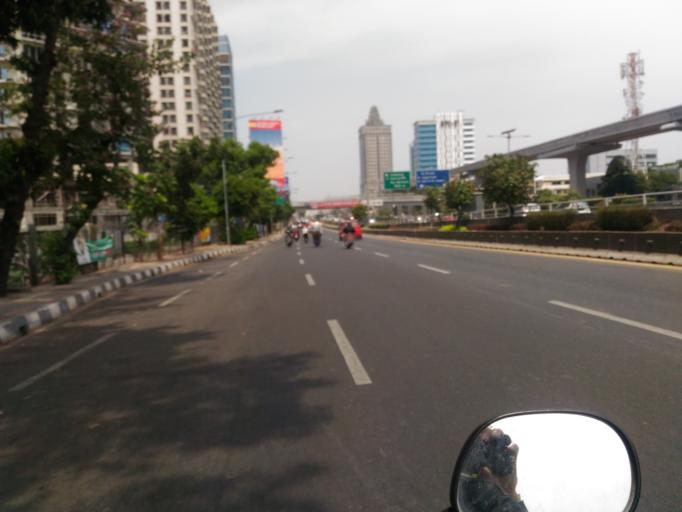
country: ID
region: Jakarta Raya
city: Jakarta
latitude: -6.2430
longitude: 106.8529
